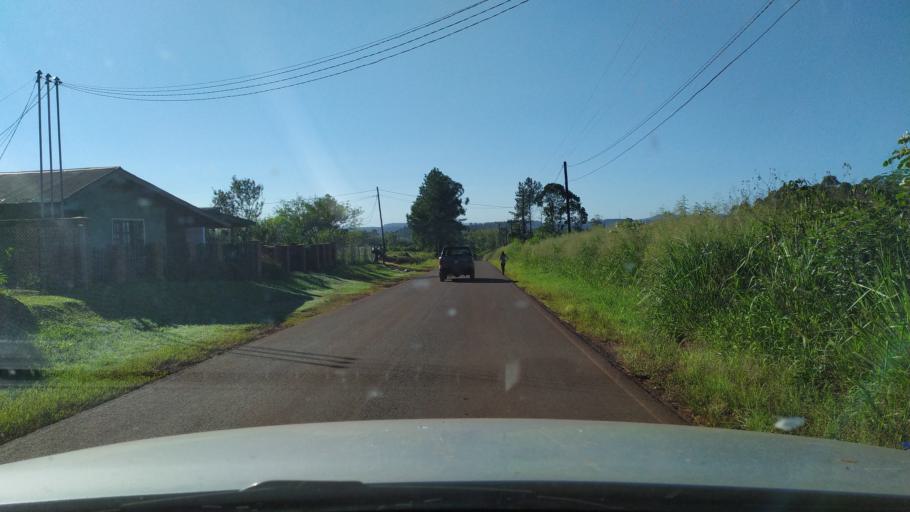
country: AR
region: Misiones
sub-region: Departamento de Montecarlo
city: Montecarlo
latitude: -26.5882
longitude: -54.7218
